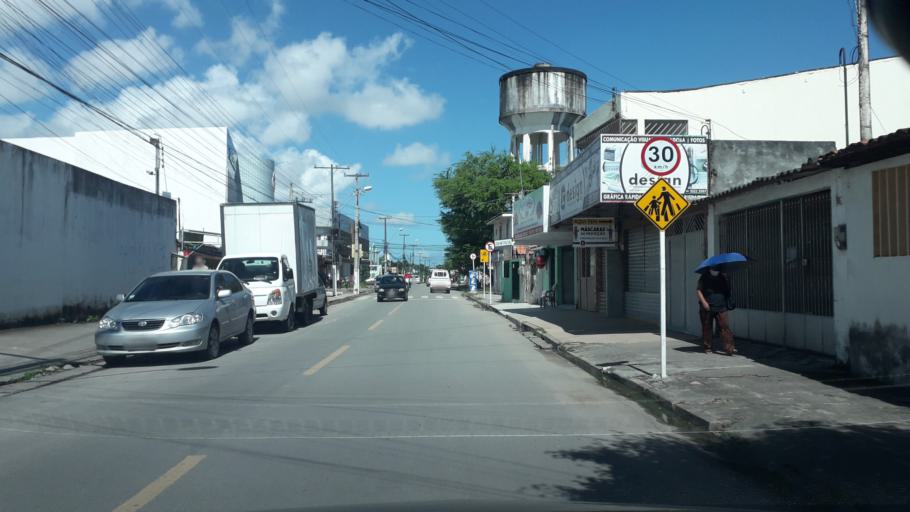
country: BR
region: Alagoas
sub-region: Satuba
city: Satuba
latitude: -9.5775
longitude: -35.7717
